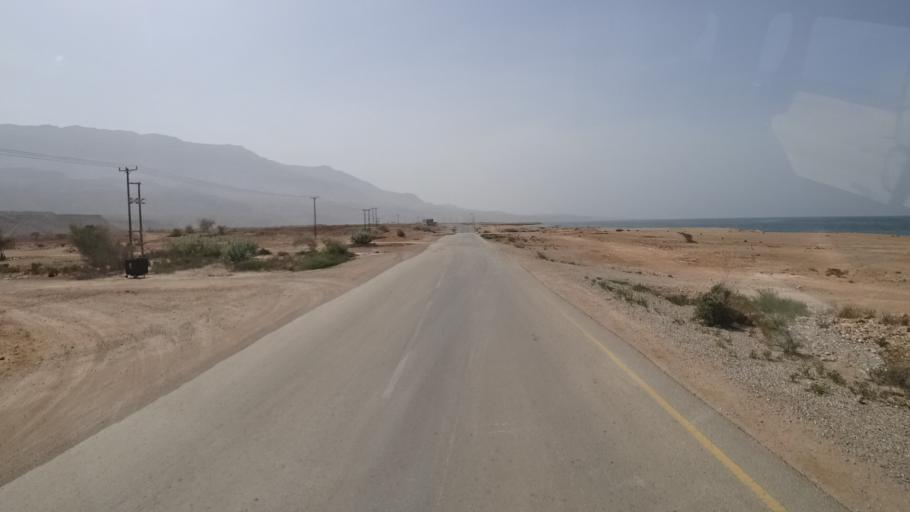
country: OM
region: Ash Sharqiyah
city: Sur
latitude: 22.9950
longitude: 59.1302
